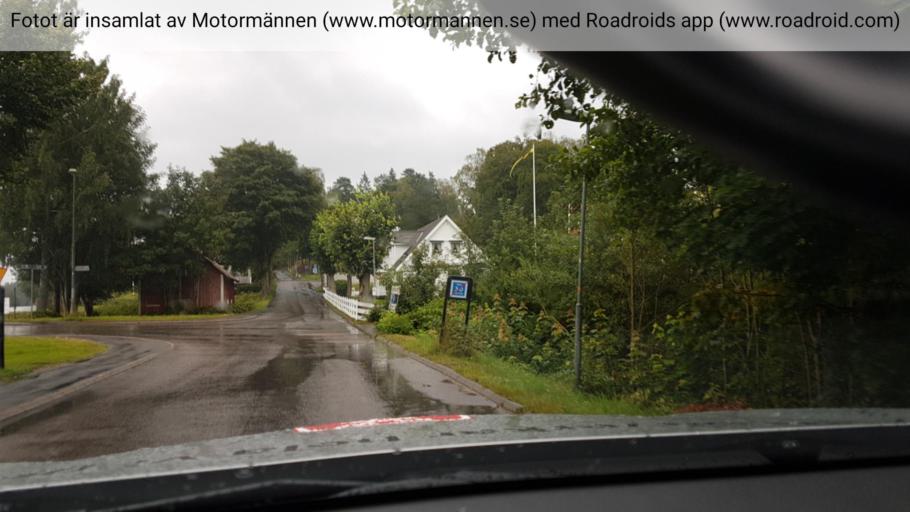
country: SE
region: Vaestra Goetaland
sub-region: Harryda Kommun
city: Hindas
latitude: 57.7048
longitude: 12.4595
